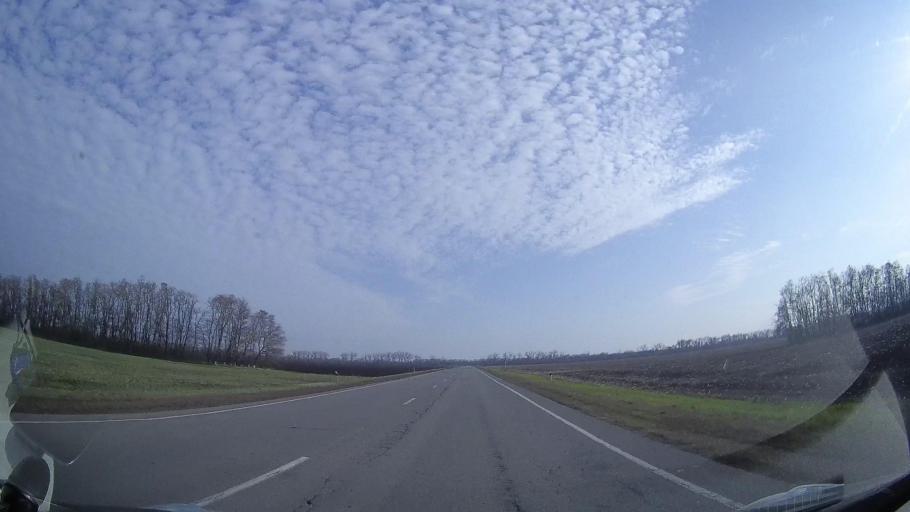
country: RU
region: Rostov
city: Tselina
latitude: 46.5223
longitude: 41.1388
